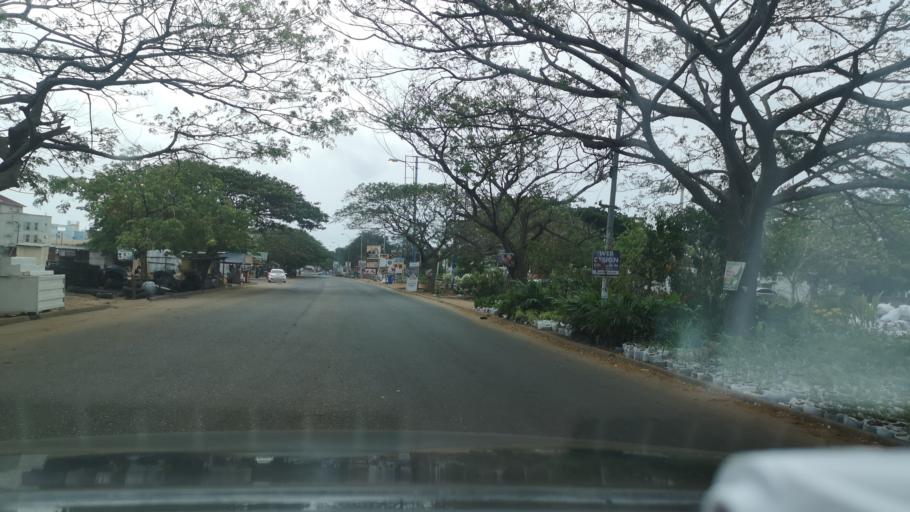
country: GH
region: Greater Accra
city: Nungua
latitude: 5.6228
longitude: -0.0651
